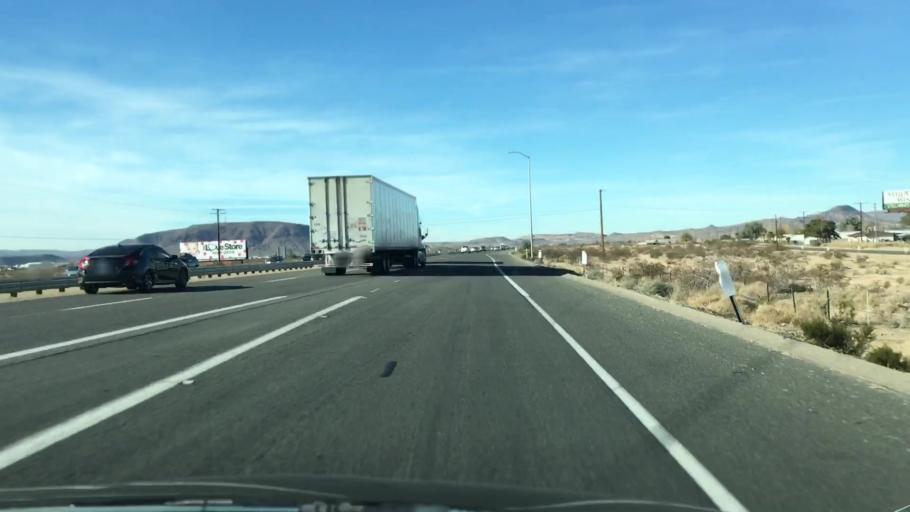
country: US
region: California
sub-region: San Bernardino County
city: Barstow
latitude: 34.9085
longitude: -116.8450
